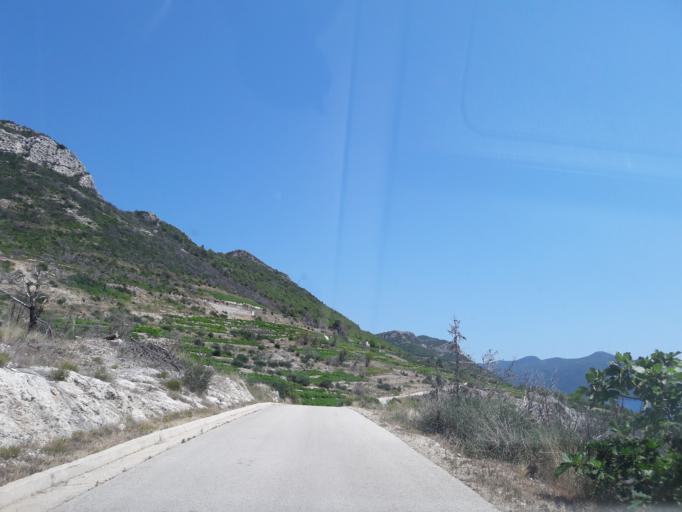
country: HR
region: Dubrovacko-Neretvanska
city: Blato
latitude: 42.9182
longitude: 17.4067
